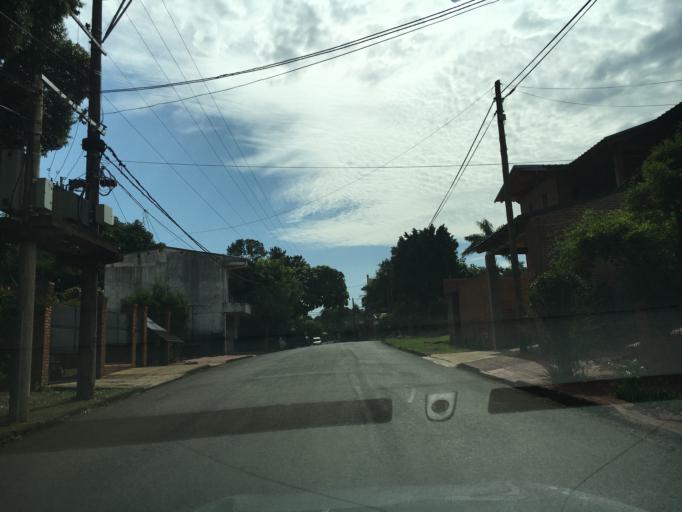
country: AR
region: Misiones
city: Puerto Rico
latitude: -26.8107
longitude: -55.0283
